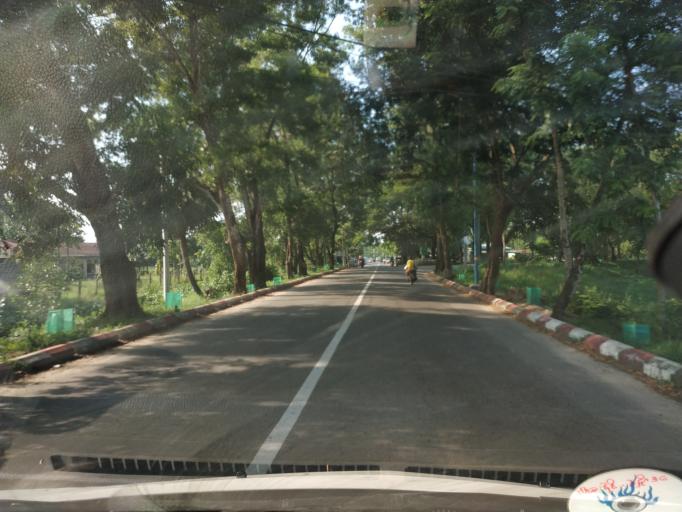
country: MM
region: Ayeyarwady
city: Pathein
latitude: 16.8121
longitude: 94.7542
